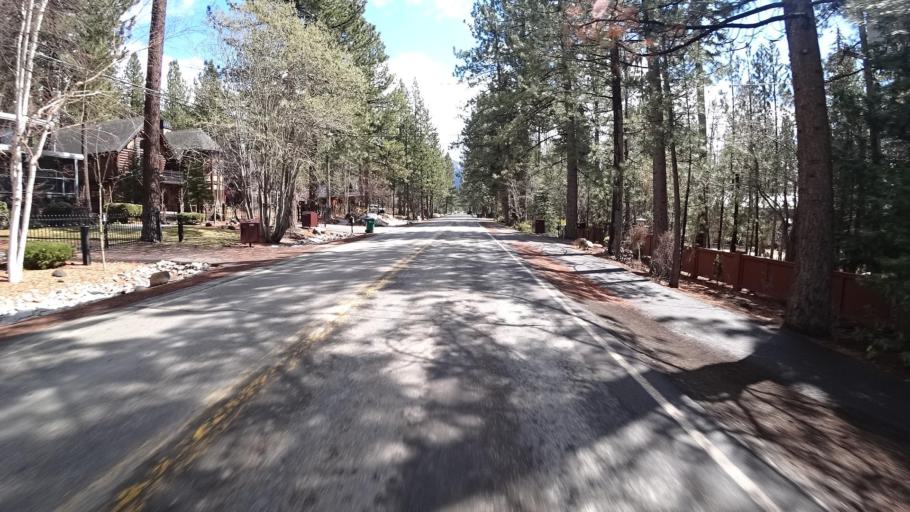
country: US
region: Nevada
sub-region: Washoe County
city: Incline Village
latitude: 39.2434
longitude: -119.9578
